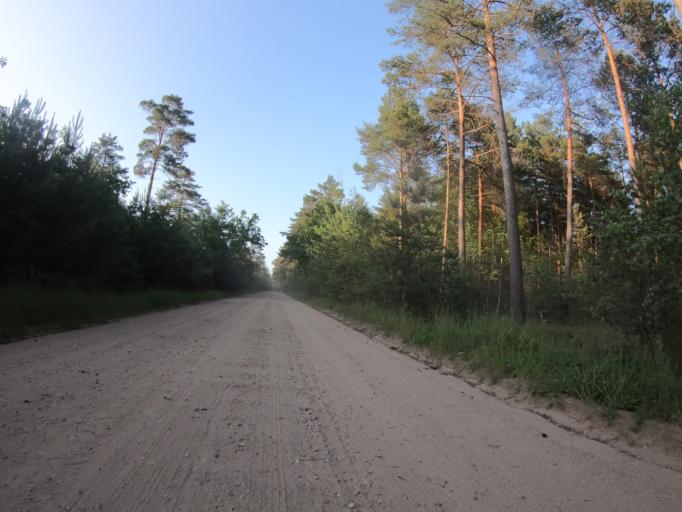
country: DE
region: Lower Saxony
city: Wagenhoff
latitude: 52.5468
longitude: 10.5037
